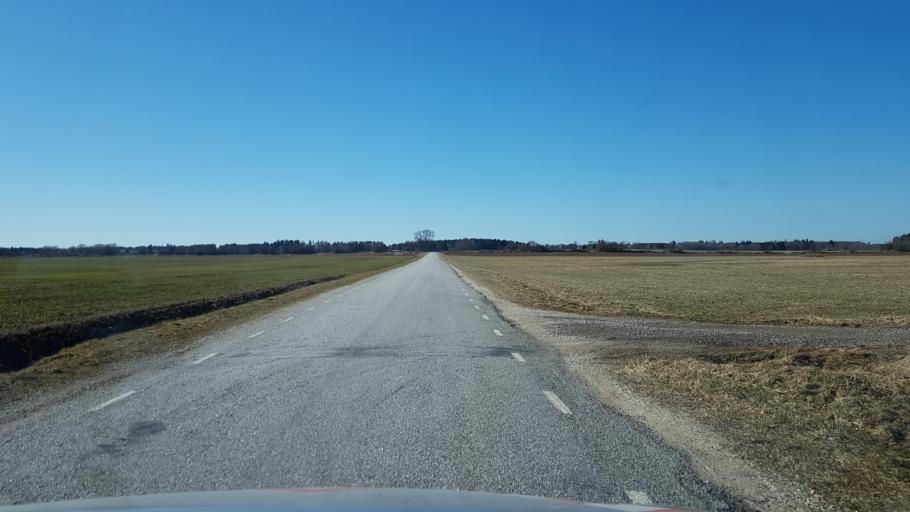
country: EE
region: Laeaene-Virumaa
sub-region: Viru-Nigula vald
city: Kunda
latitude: 59.3986
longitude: 26.5550
